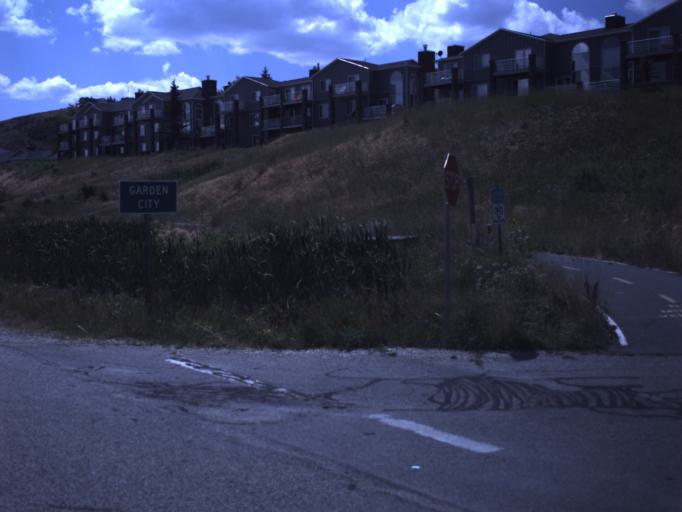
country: US
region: Idaho
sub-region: Bear Lake County
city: Paris
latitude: 41.9645
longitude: -111.3998
